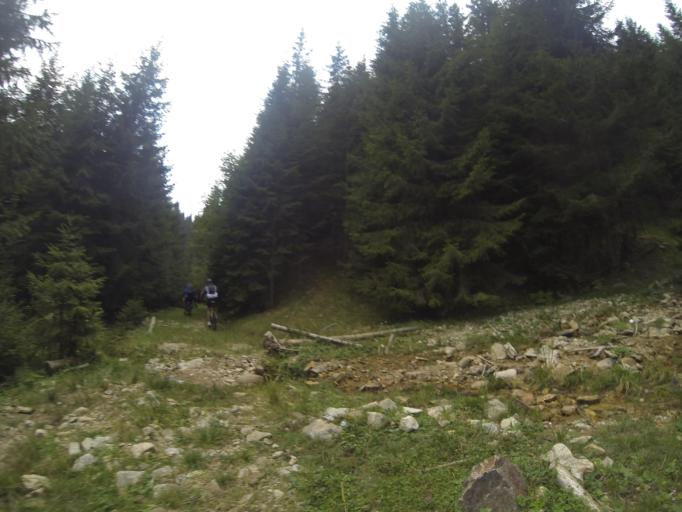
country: RO
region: Gorj
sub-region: Comuna Polovragi
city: Polovragi
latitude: 45.2825
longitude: 23.8386
